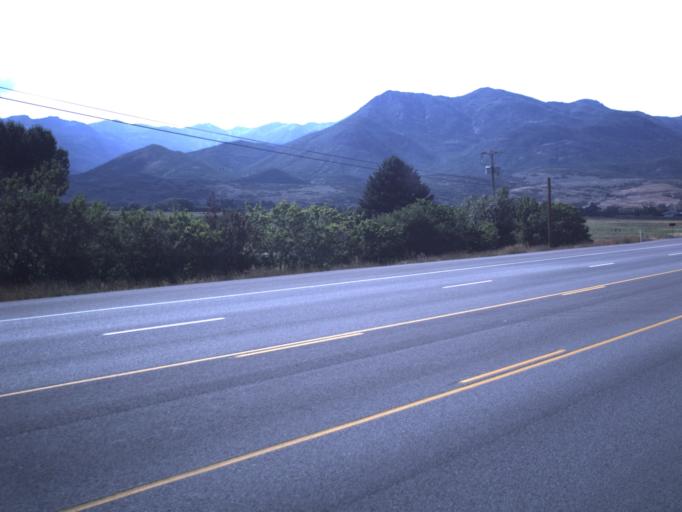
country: US
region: Utah
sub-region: Wasatch County
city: Heber
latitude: 40.5360
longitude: -111.4105
